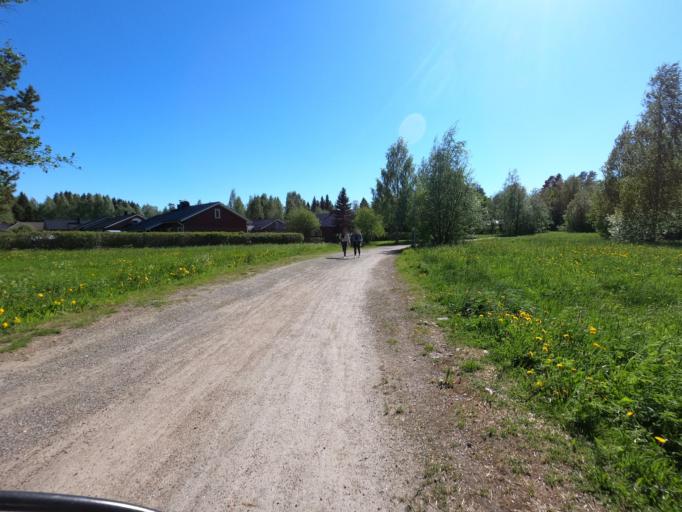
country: FI
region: North Karelia
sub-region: Joensuu
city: Joensuu
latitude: 62.5887
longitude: 29.8002
